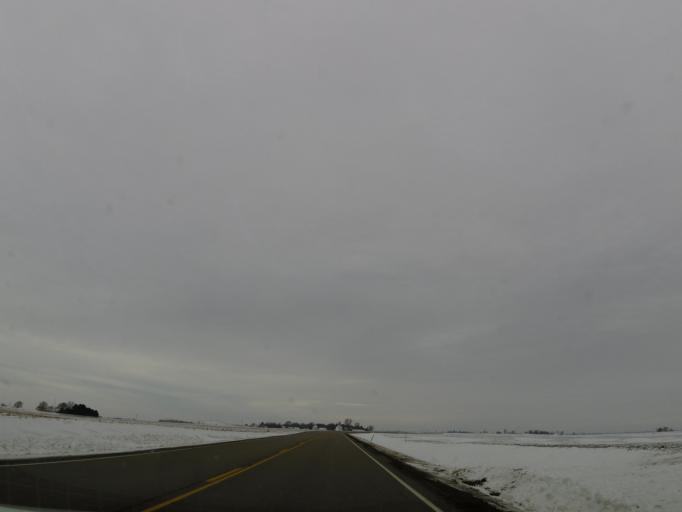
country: US
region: Illinois
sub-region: Putnam County
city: Granville
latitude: 41.2576
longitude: -89.1571
